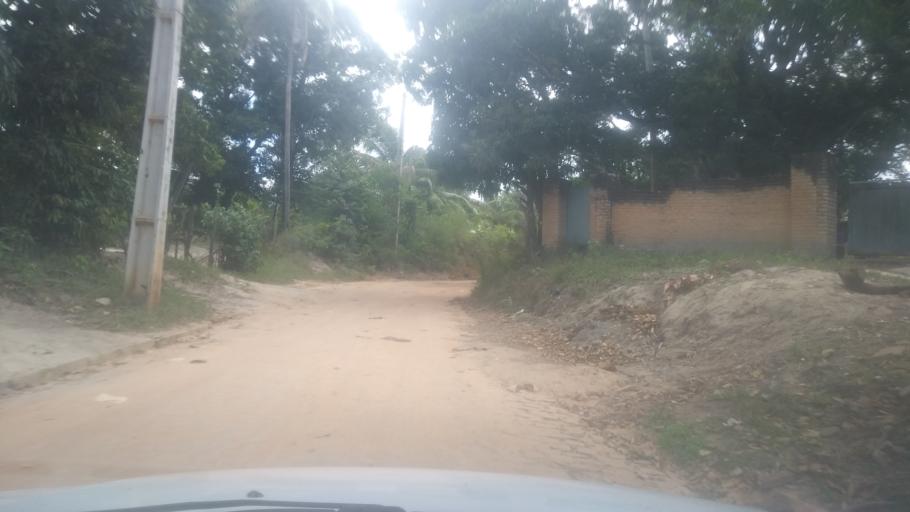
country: BR
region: Rio Grande do Norte
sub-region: Sao Jose De Mipibu
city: Sao Jose de Mipibu
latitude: -6.0711
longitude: -35.2269
